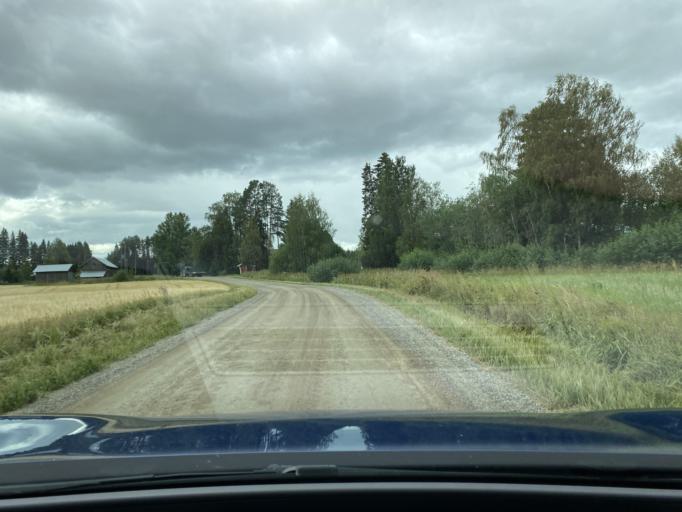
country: FI
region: Pirkanmaa
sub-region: Lounais-Pirkanmaa
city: Punkalaidun
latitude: 61.1811
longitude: 23.1831
